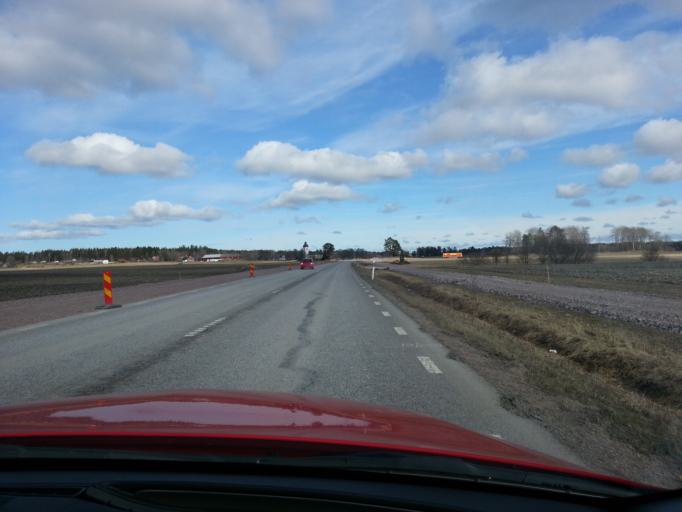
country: SE
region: Uppsala
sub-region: Osthammars Kommun
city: Gimo
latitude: 60.0528
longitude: 18.0563
